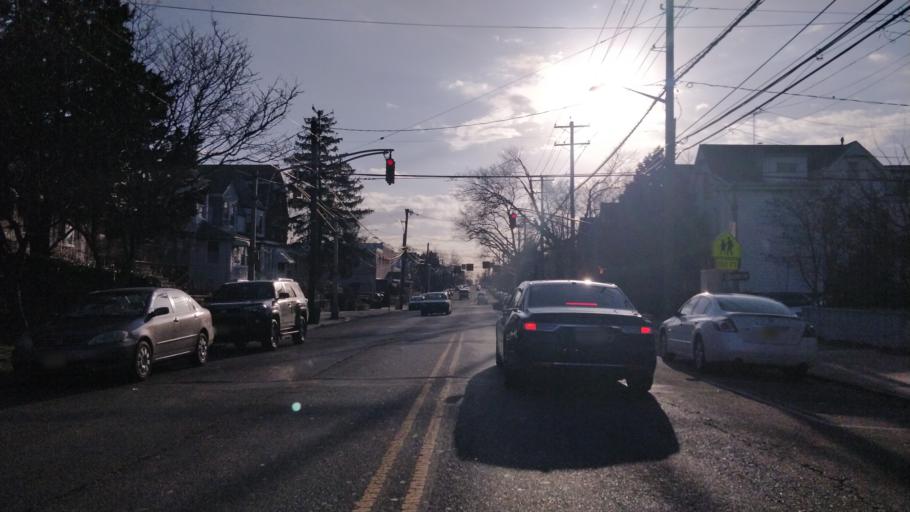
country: US
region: New Jersey
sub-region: Hudson County
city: Bayonne
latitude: 40.6721
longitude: -74.1082
